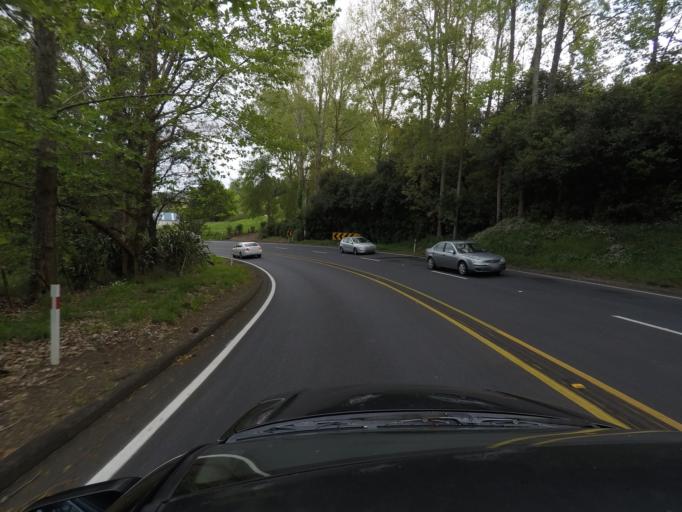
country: NZ
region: Auckland
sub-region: Auckland
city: Pakuranga
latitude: -36.9242
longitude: 174.9331
